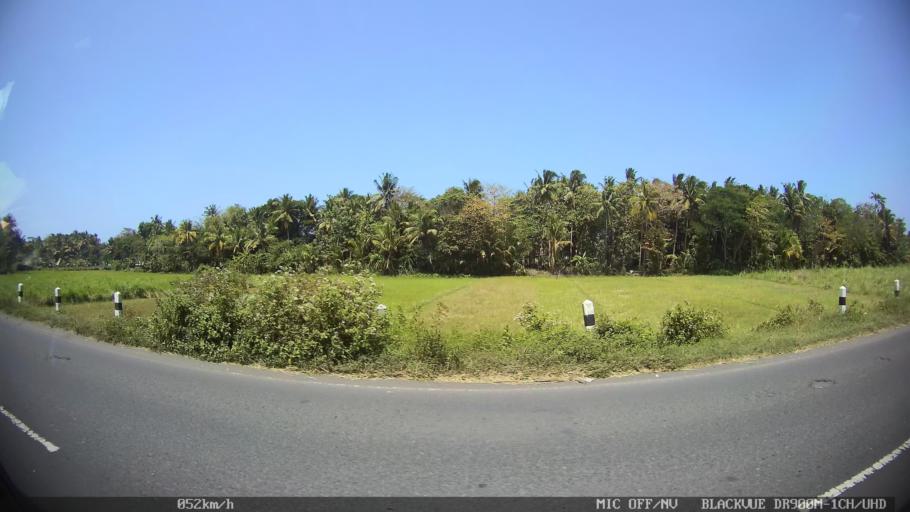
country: ID
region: Daerah Istimewa Yogyakarta
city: Srandakan
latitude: -7.9439
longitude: 110.1711
